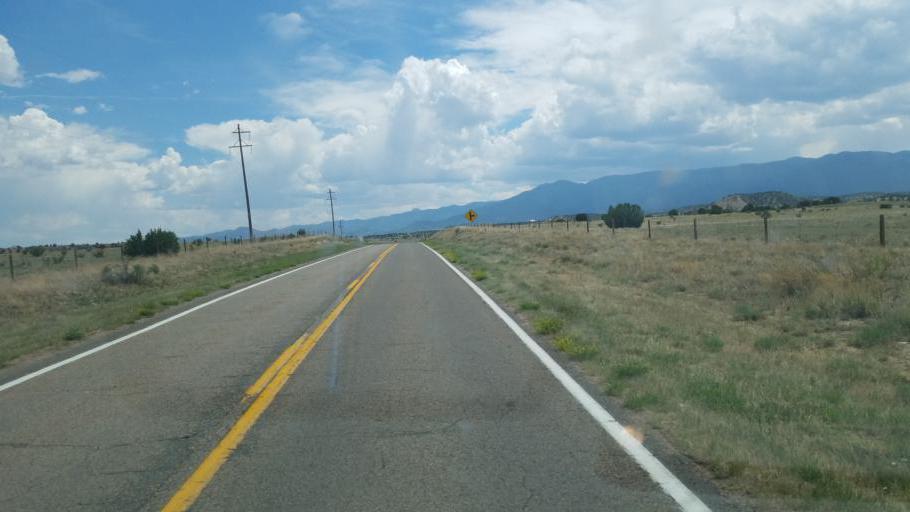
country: US
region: Colorado
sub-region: Fremont County
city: Florence
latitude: 38.3449
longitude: -105.1071
